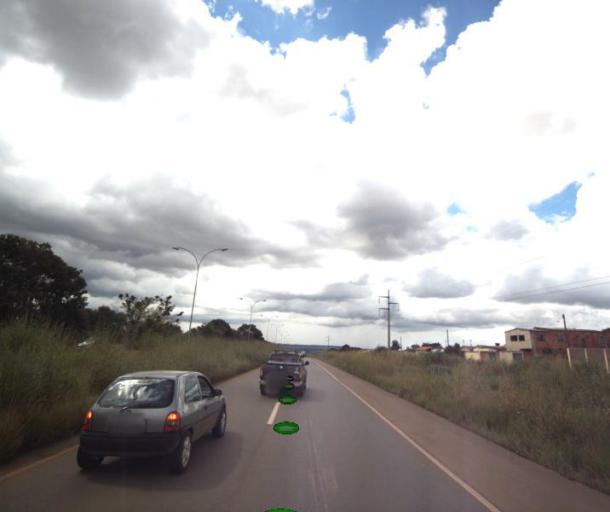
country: BR
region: Goias
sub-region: Anapolis
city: Anapolis
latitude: -16.3328
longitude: -48.9224
